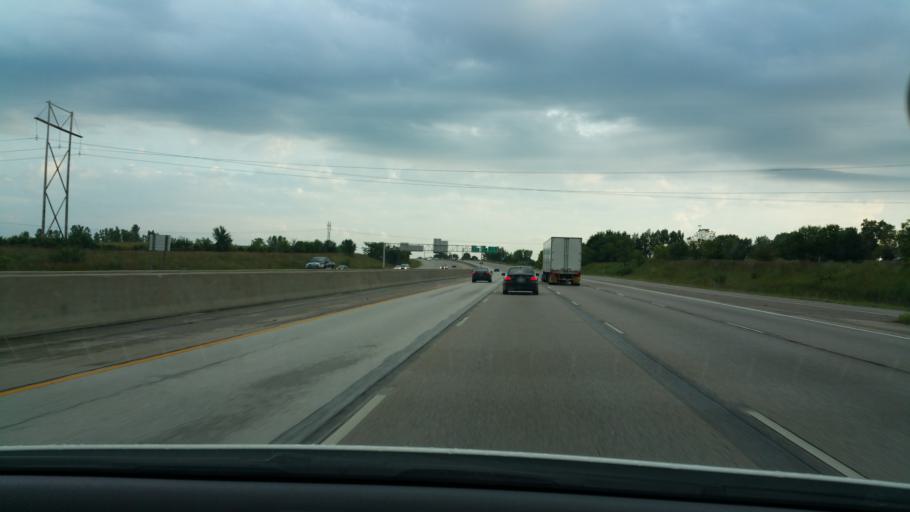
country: US
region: Iowa
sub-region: Polk County
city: Saylorville
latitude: 41.6766
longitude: -93.5776
